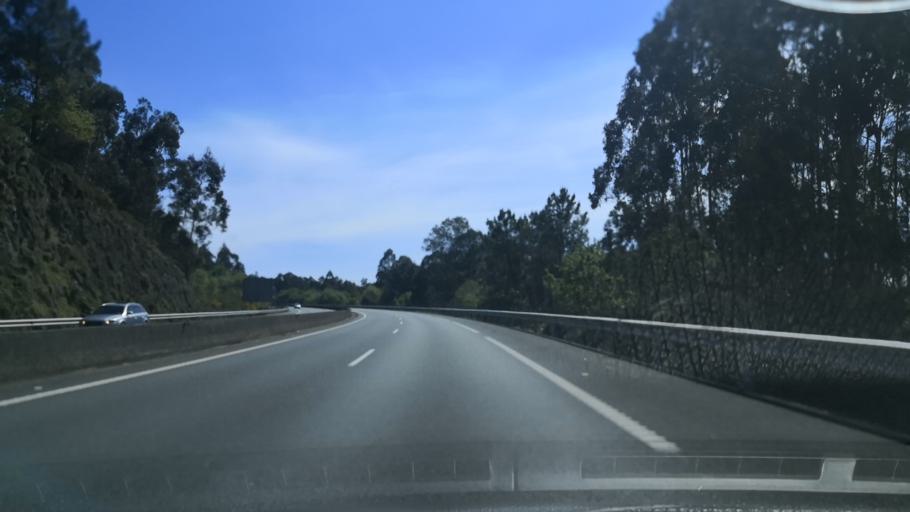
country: ES
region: Galicia
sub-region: Provincia da Coruna
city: Santiago de Compostela
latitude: 42.8463
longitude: -8.5719
